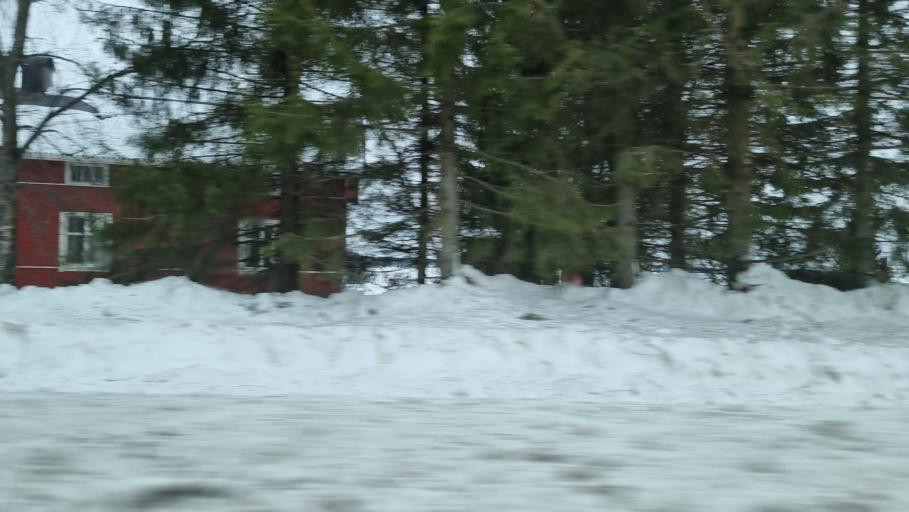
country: FI
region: Lapland
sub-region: Kemi-Tornio
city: Tornio
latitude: 65.9831
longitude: 24.0684
